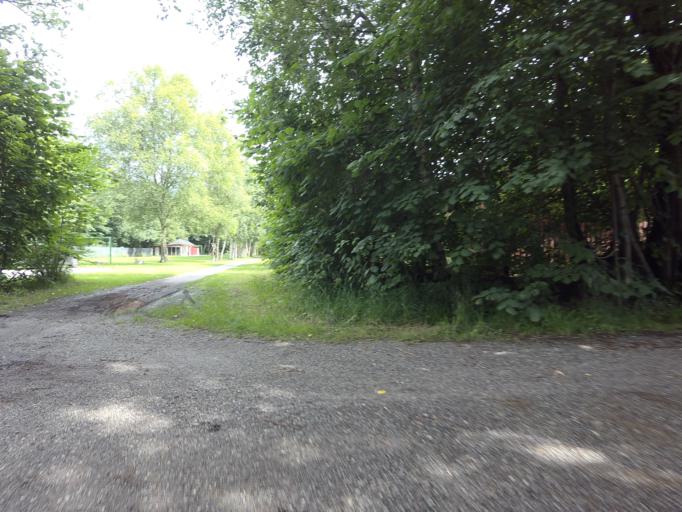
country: DK
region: Central Jutland
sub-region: Favrskov Kommune
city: Hammel
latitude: 56.3190
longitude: 9.8714
